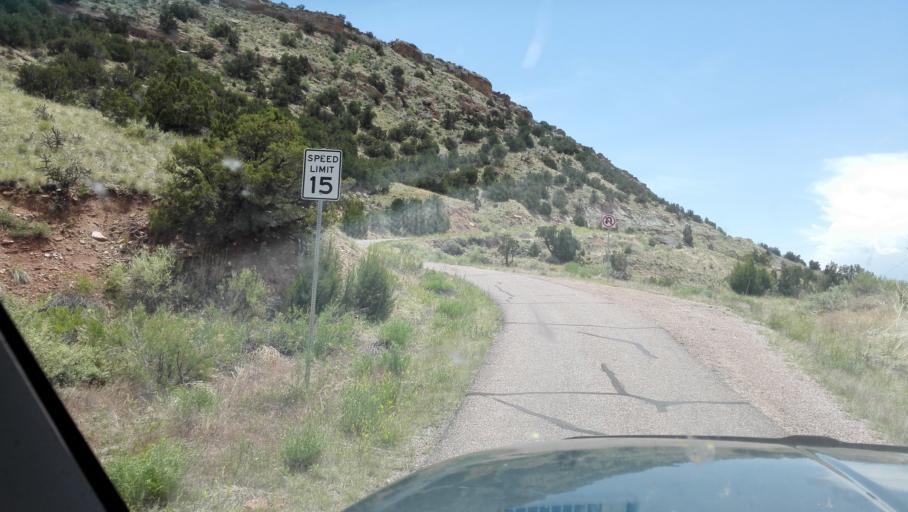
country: US
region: Colorado
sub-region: Fremont County
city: Canon City
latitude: 38.4723
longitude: -105.2570
